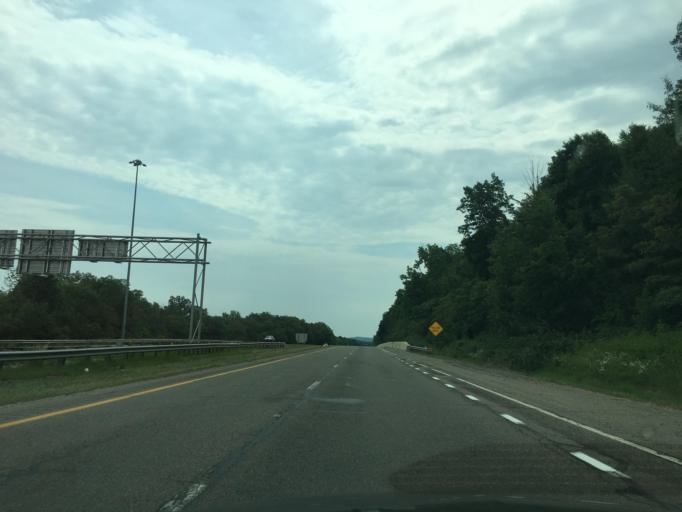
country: US
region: Ohio
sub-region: Tuscarawas County
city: New Philadelphia
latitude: 40.4900
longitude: -81.4760
